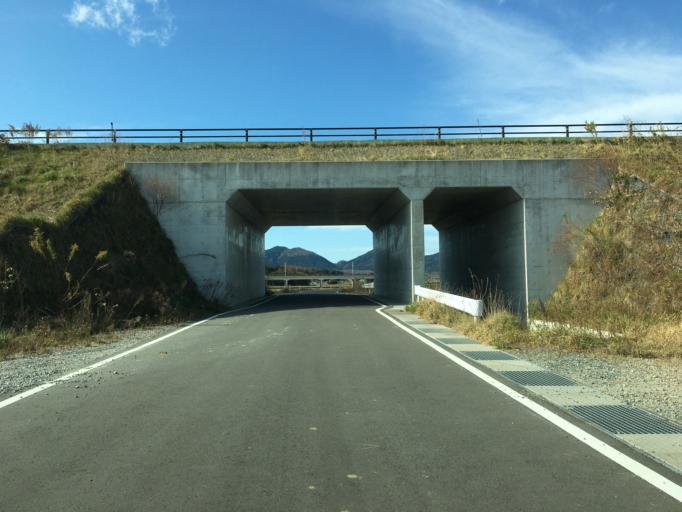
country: JP
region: Miyagi
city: Marumori
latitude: 37.8886
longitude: 140.9262
